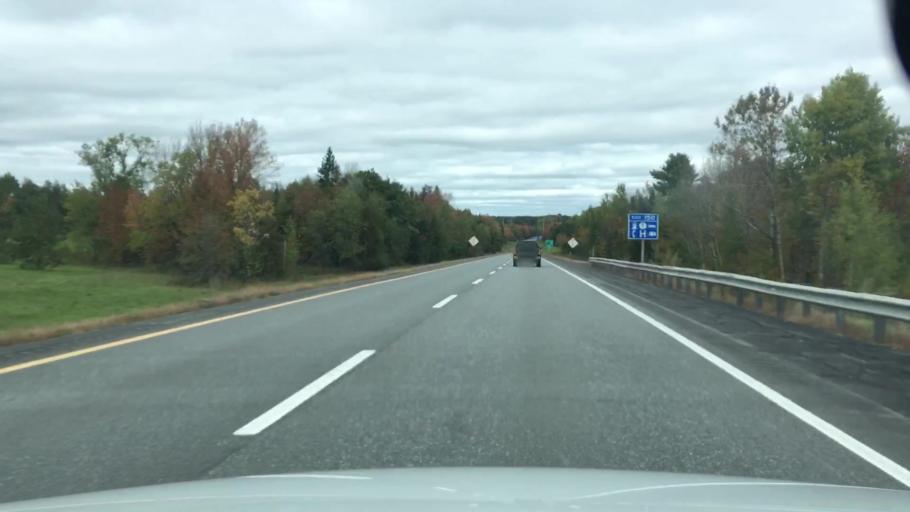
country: US
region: Maine
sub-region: Somerset County
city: Pittsfield
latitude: 44.7704
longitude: -69.4097
